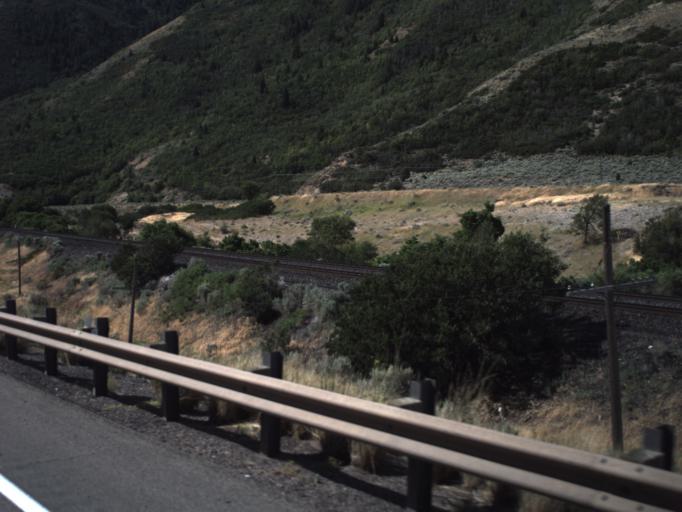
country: US
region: Utah
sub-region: Utah County
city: Mapleton
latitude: 40.0697
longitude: -111.5756
